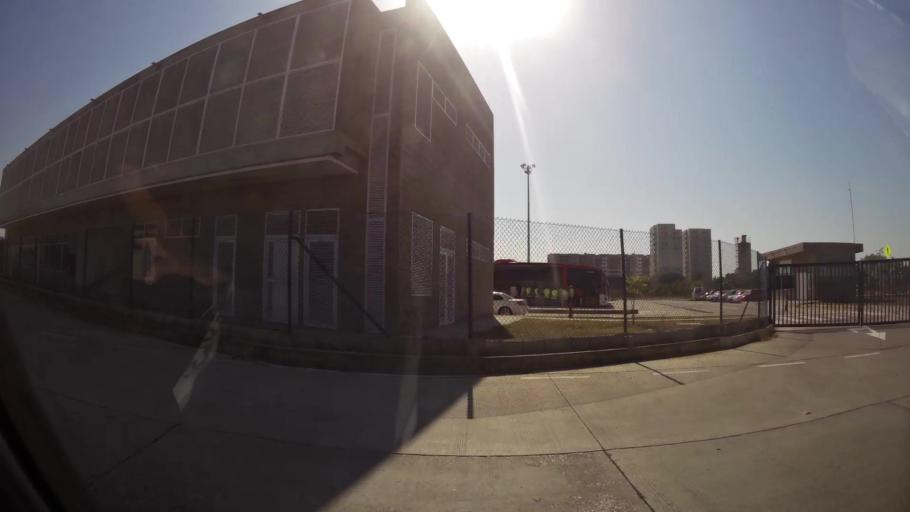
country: CO
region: Bolivar
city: Cartagena
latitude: 10.3932
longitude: -75.4706
